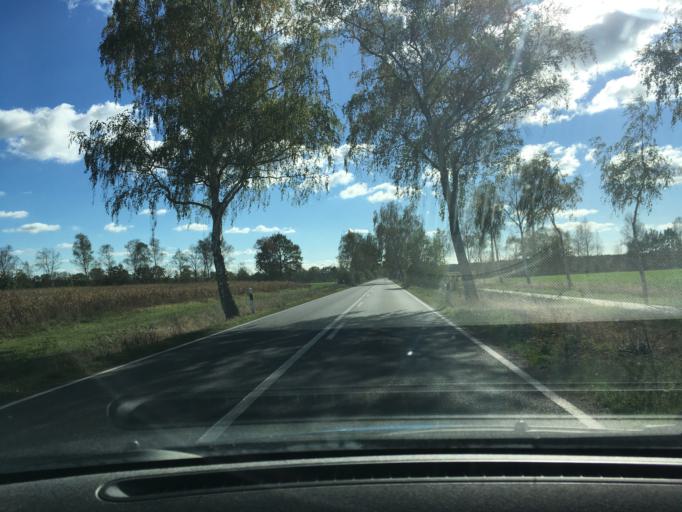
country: DE
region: Lower Saxony
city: Isernhagen Farster Bauerschaft
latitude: 52.5582
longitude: 9.8538
